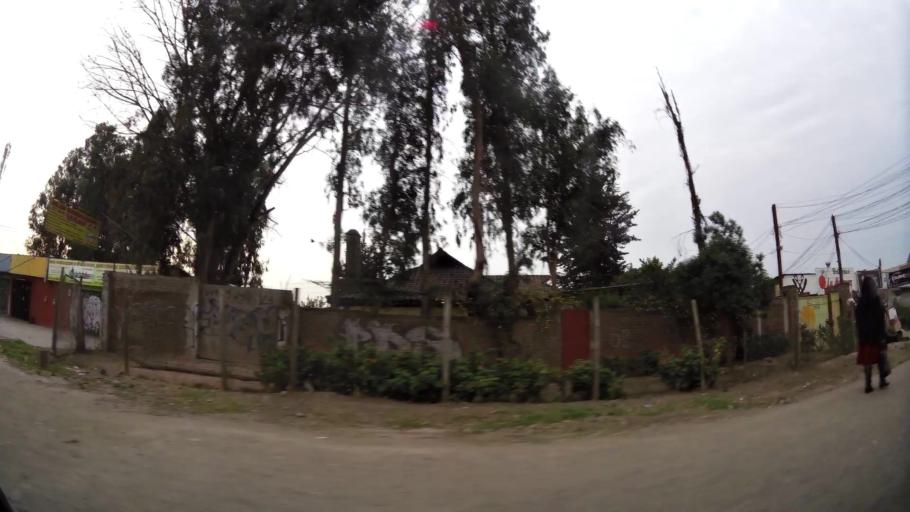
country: CL
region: Santiago Metropolitan
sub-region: Provincia de Santiago
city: Lo Prado
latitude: -33.5186
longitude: -70.7882
